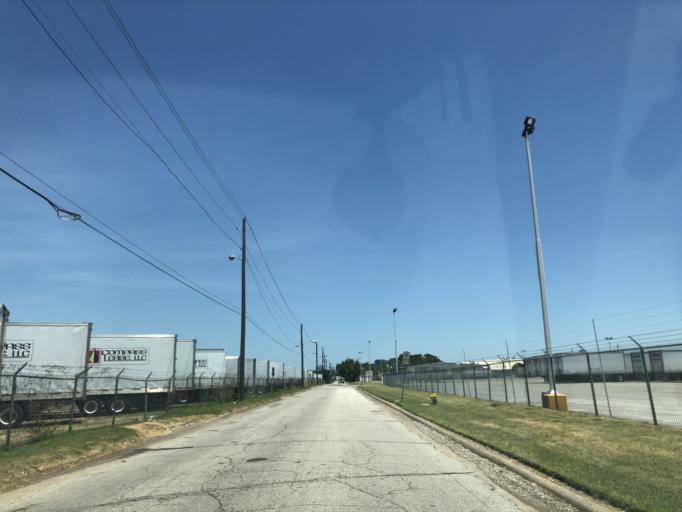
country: US
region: Texas
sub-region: Dallas County
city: Irving
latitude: 32.8126
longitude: -96.8891
